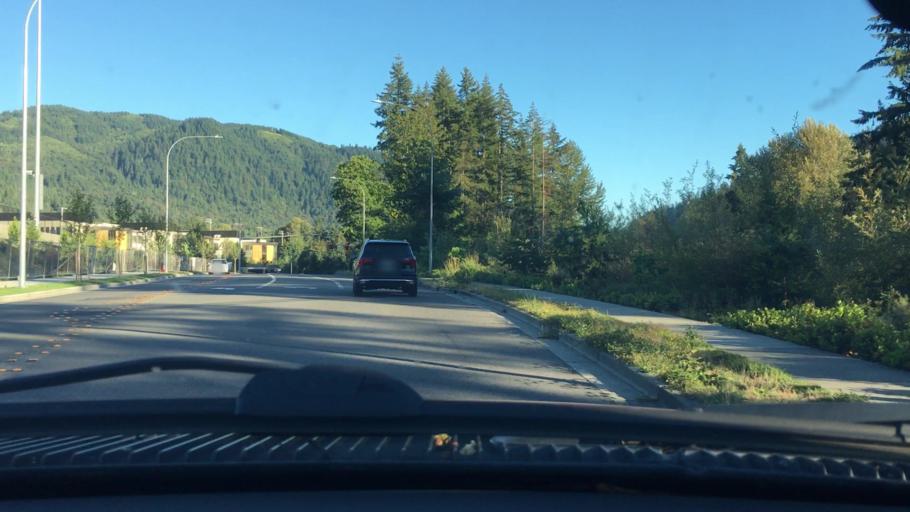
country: US
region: Washington
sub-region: King County
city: Issaquah
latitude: 47.5244
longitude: -122.0318
